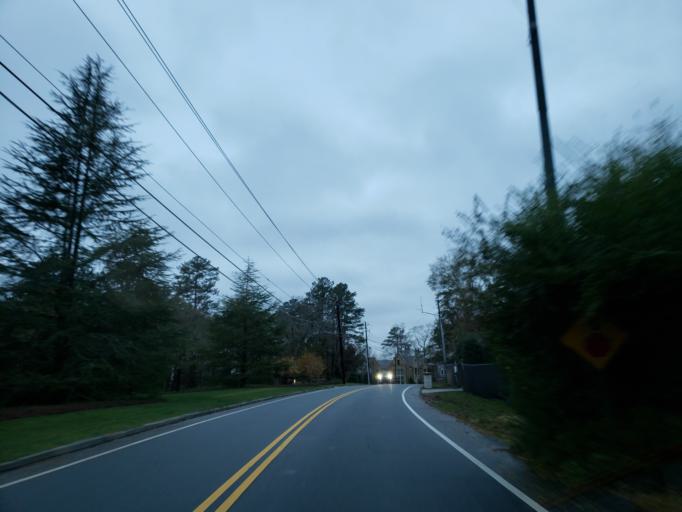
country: US
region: Georgia
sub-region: Cobb County
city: Vinings
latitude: 33.8804
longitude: -84.4227
